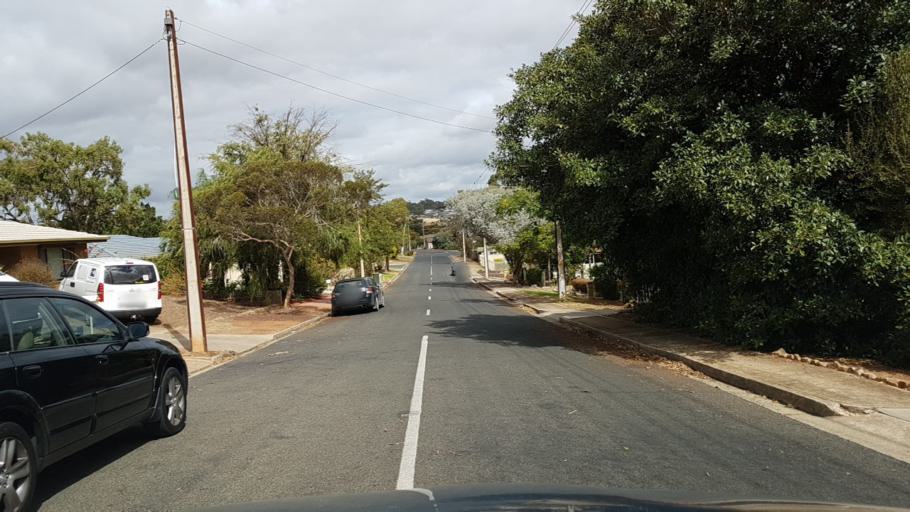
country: AU
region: South Australia
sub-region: Gawler
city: Gawler
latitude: -34.6073
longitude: 138.7542
